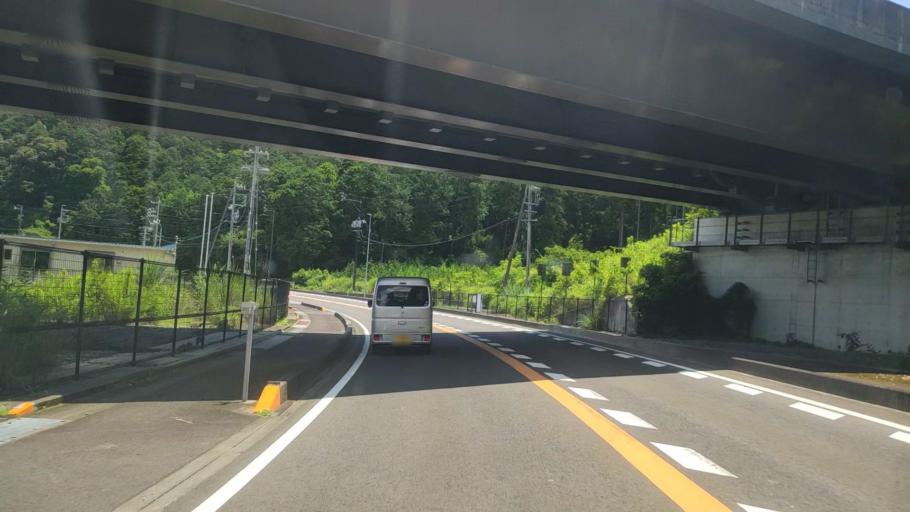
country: JP
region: Mie
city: Owase
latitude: 34.1160
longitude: 136.2197
